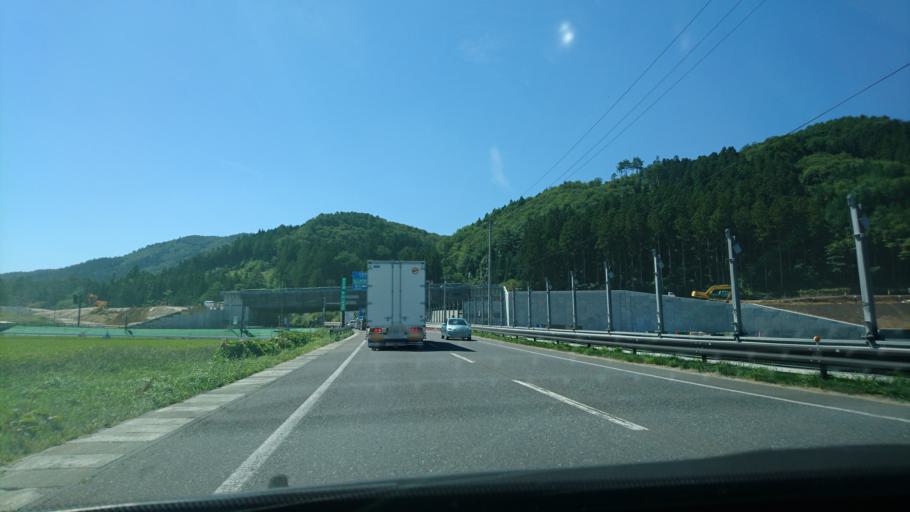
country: JP
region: Iwate
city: Tono
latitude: 39.2672
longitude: 141.5873
